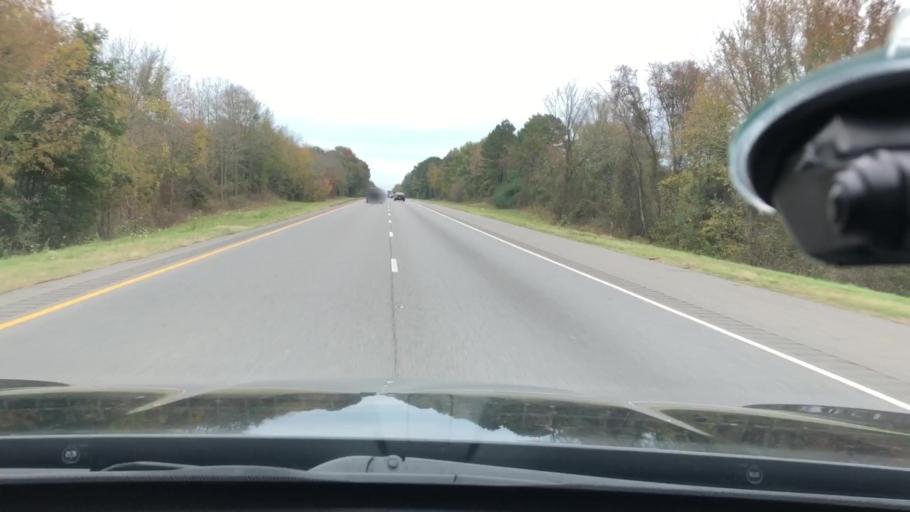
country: US
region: Arkansas
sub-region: Hempstead County
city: Hope
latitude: 33.6403
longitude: -93.6978
